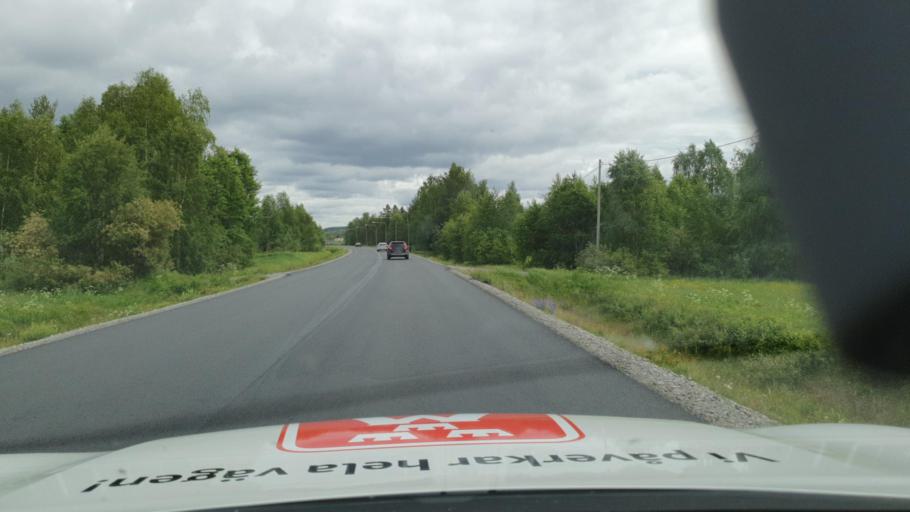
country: SE
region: Vaesterbotten
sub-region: Asele Kommun
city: Asele
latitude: 64.1647
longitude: 17.3244
